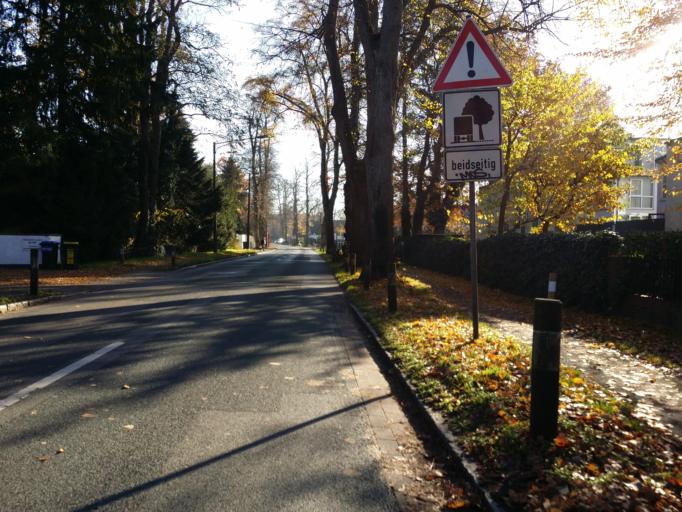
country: DE
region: Lower Saxony
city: Lilienthal
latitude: 53.0820
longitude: 8.9376
